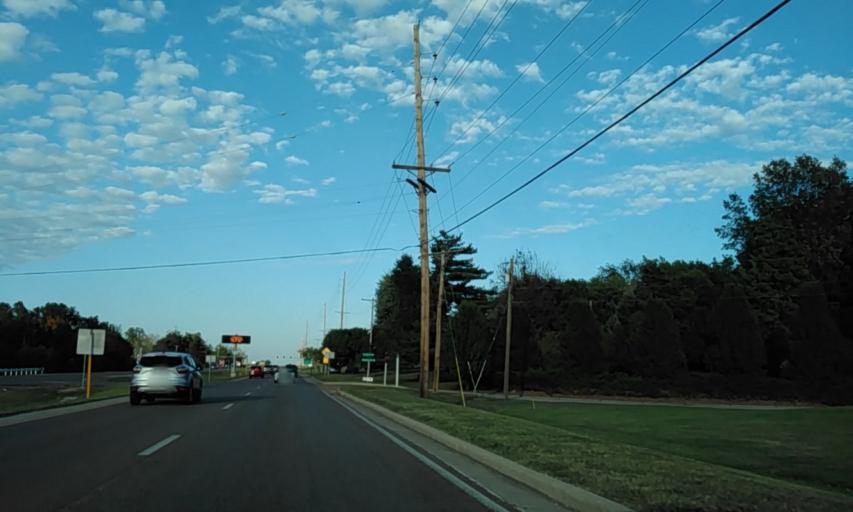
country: US
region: Missouri
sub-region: Saint Louis County
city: Sappington
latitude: 38.5275
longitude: -90.3926
